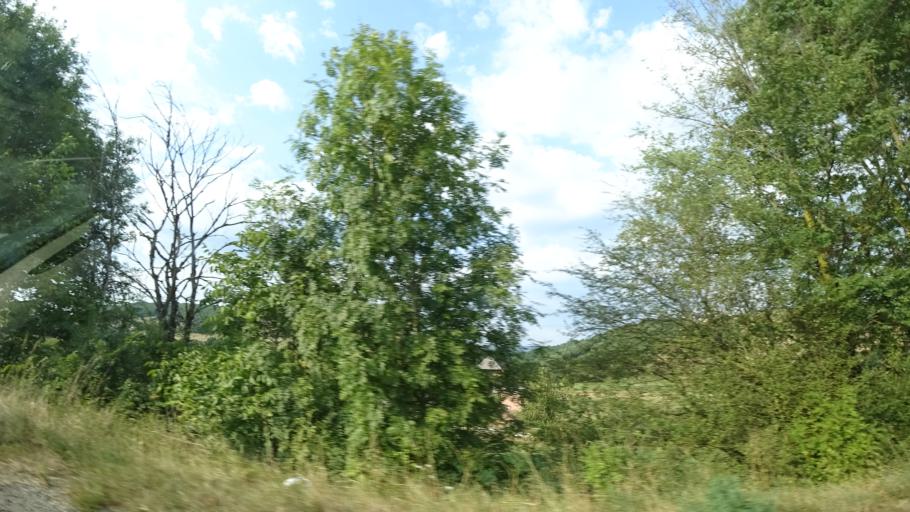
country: FR
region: Midi-Pyrenees
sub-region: Departement de l'Aveyron
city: Saint-Christophe-Vallon
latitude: 44.4957
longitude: 2.3856
